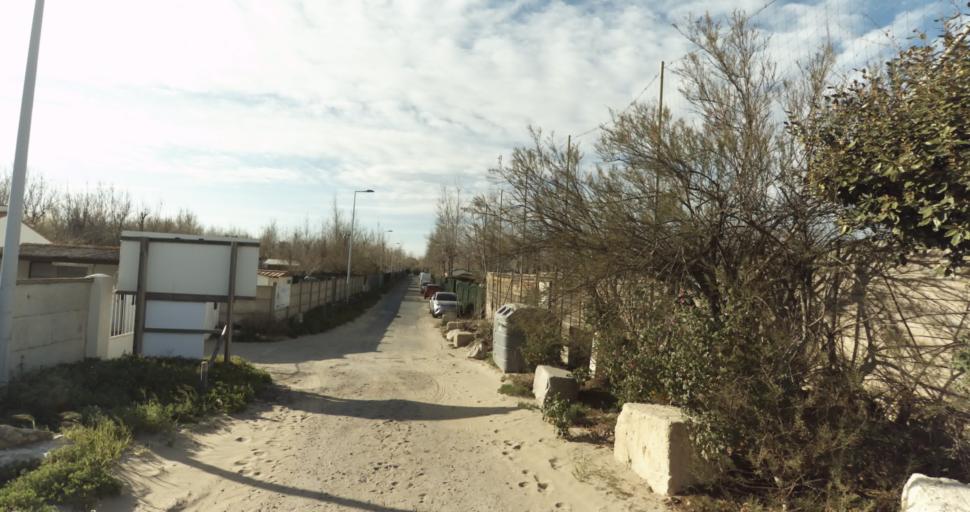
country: FR
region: Languedoc-Roussillon
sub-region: Departement de l'Herault
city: Le Cap d'Agde
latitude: 43.3072
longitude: 3.5435
